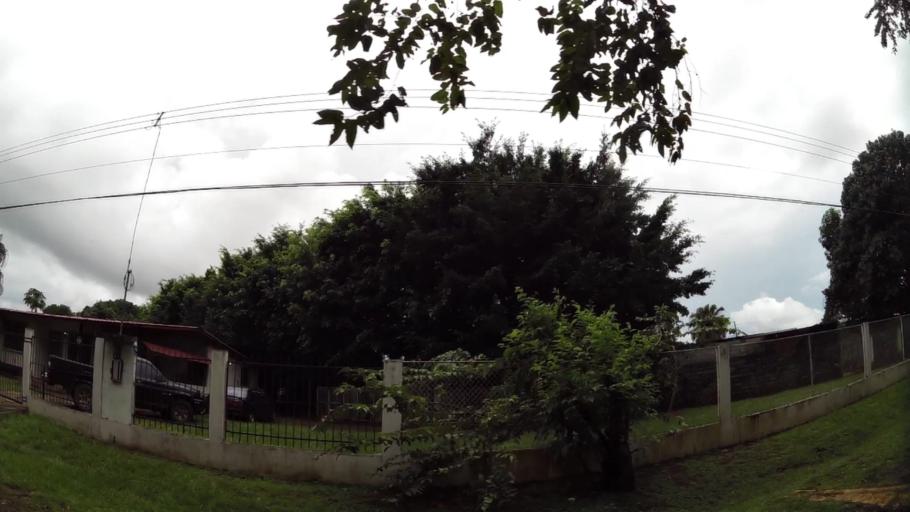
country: PA
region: Chiriqui
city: David
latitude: 8.4166
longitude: -82.4568
